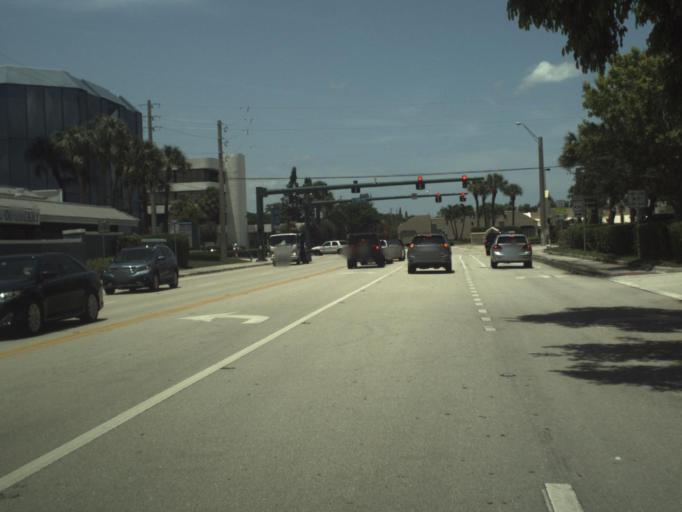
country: US
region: Florida
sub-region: Martin County
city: Sewall's Point
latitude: 27.1965
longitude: -80.2241
